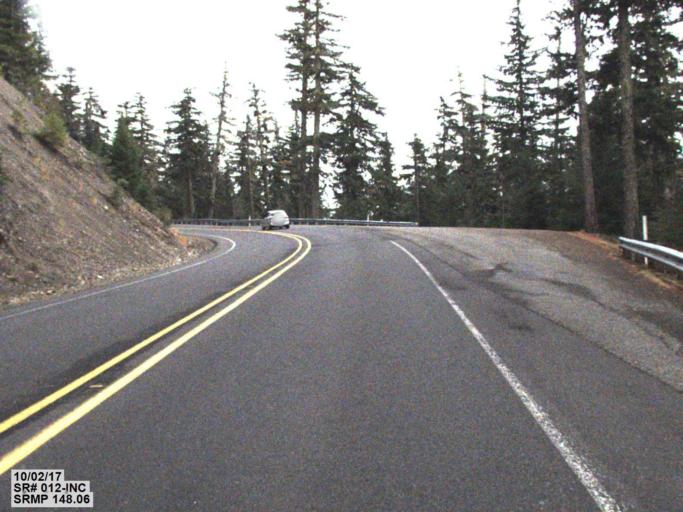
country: US
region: Washington
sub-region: Yakima County
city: Tieton
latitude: 46.6268
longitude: -121.4456
